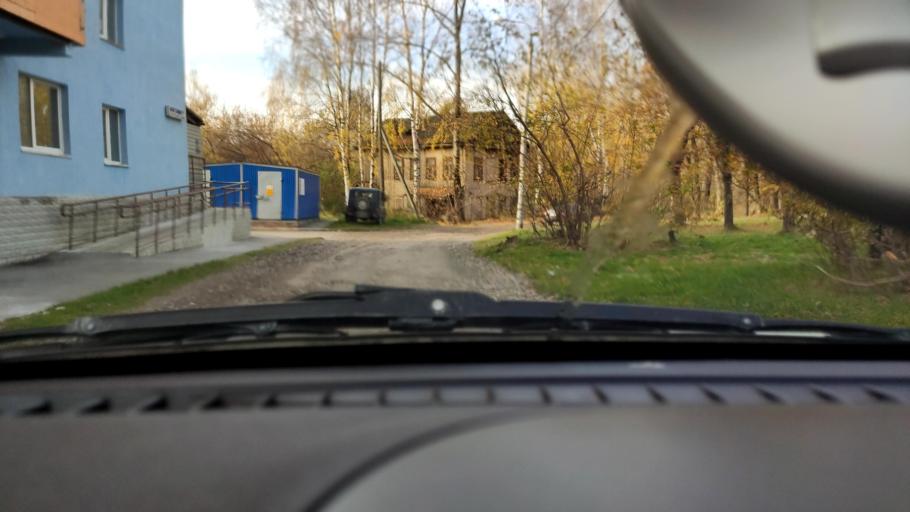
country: RU
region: Perm
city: Polazna
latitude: 58.1248
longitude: 56.3860
